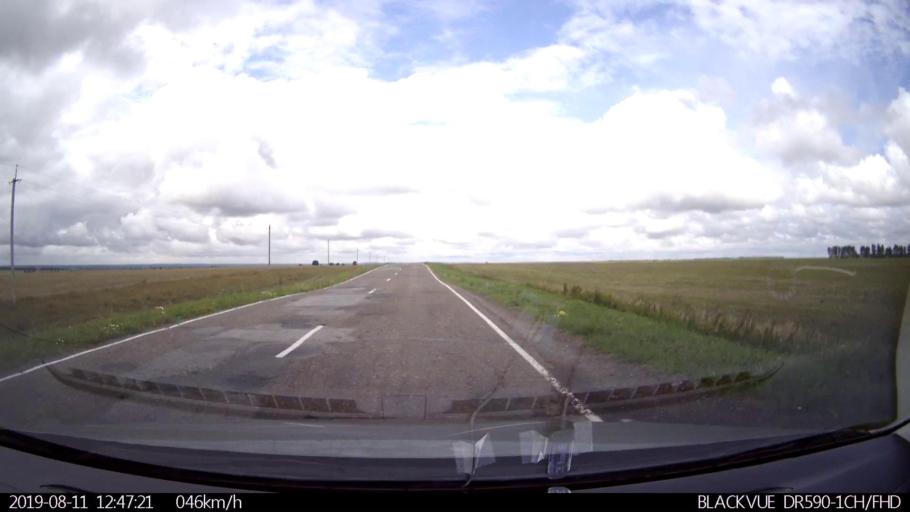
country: RU
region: Ulyanovsk
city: Ignatovka
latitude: 53.8690
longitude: 47.7095
